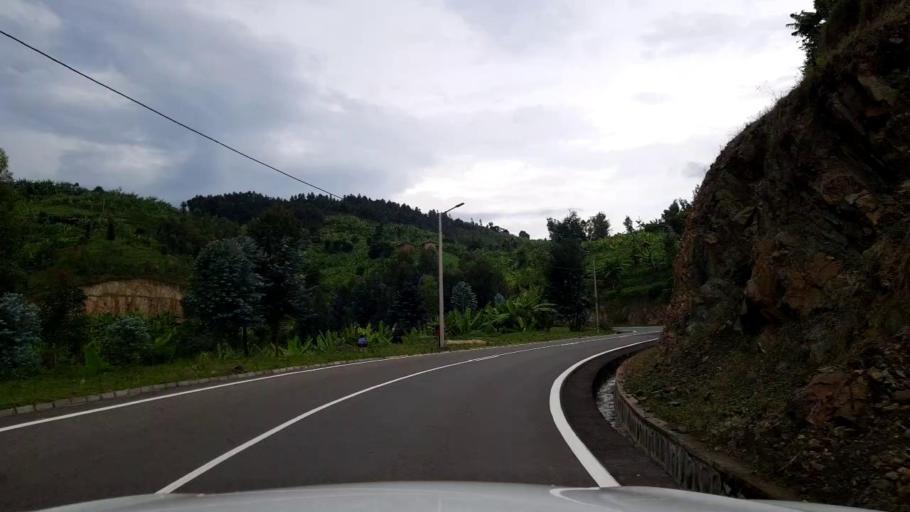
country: RW
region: Western Province
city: Kibuye
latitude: -2.0288
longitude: 29.3948
